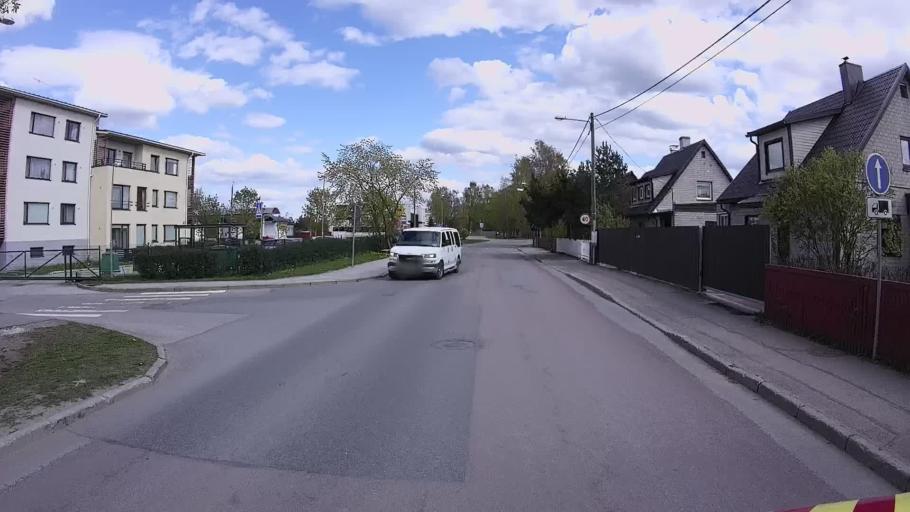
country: EE
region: Tartu
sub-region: Tartu linn
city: Tartu
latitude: 58.4010
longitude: 26.7263
